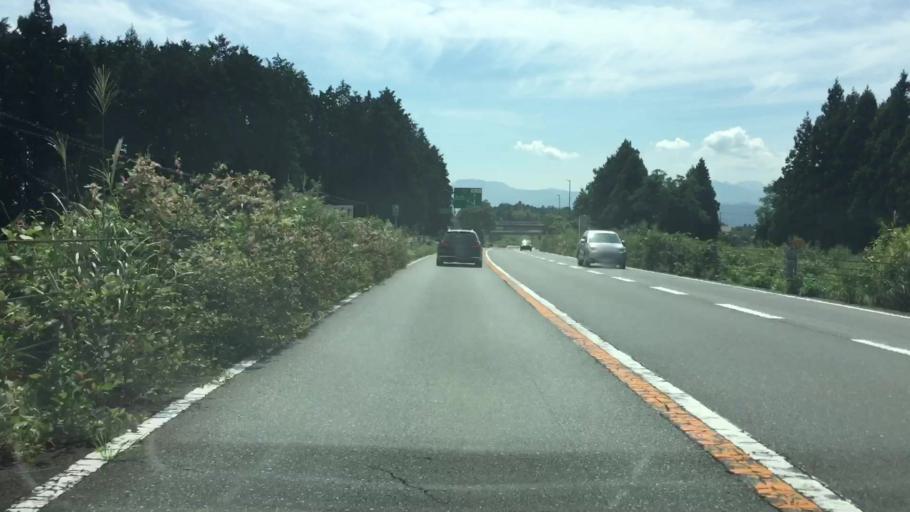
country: JP
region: Shizuoka
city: Fujinomiya
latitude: 35.2810
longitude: 138.6127
